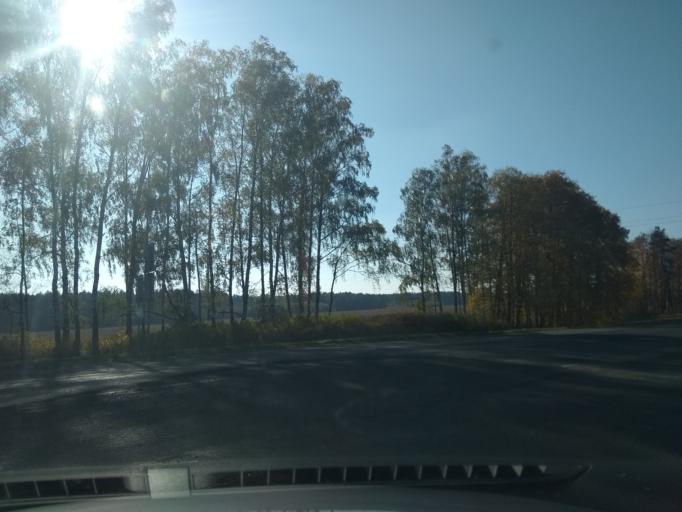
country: BY
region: Grodnenskaya
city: Zhyrovichy
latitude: 53.0570
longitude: 25.4738
